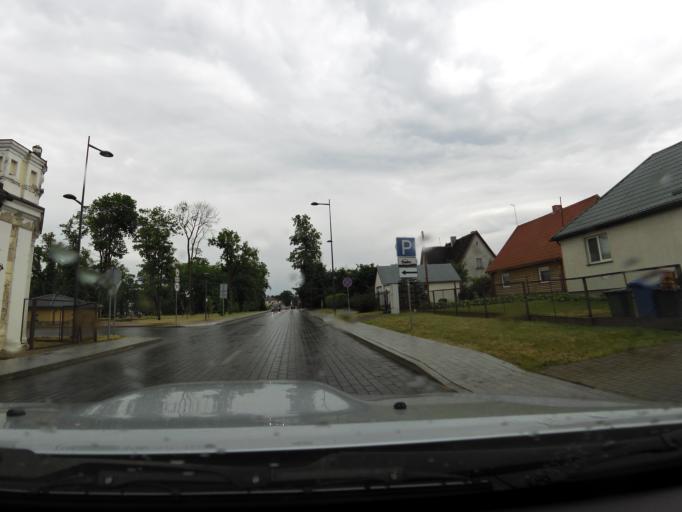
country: LT
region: Marijampoles apskritis
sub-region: Marijampole Municipality
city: Marijampole
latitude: 54.5539
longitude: 23.3445
